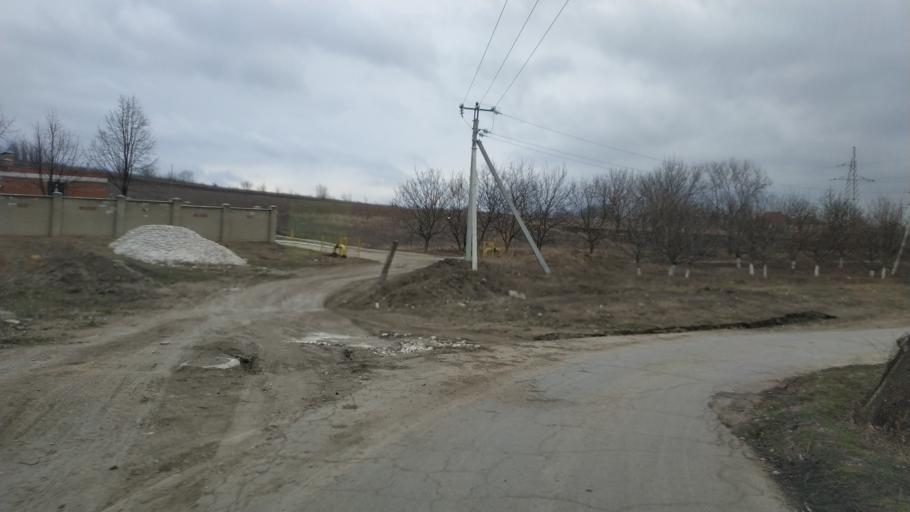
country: MD
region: Laloveni
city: Ialoveni
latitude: 46.9405
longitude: 28.7940
